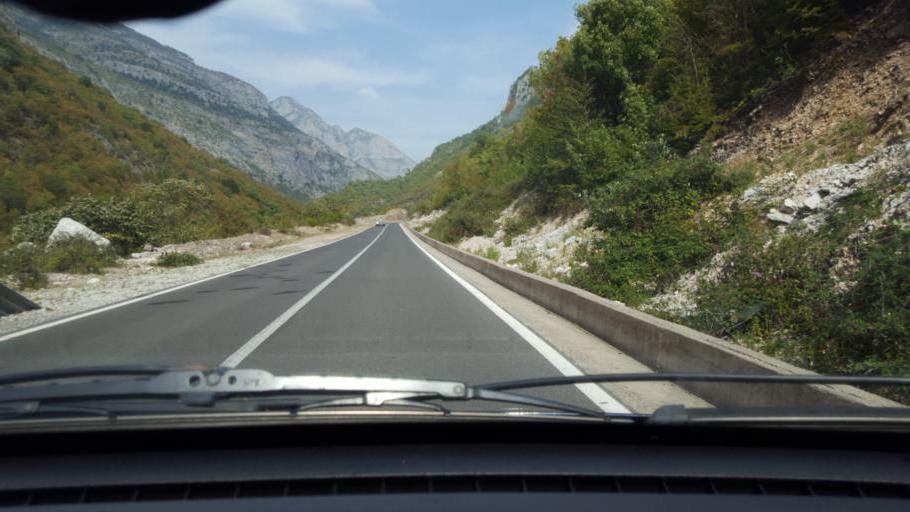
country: AL
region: Shkoder
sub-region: Rrethi i Malesia e Madhe
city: Kastrat
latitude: 42.4321
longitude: 19.5341
